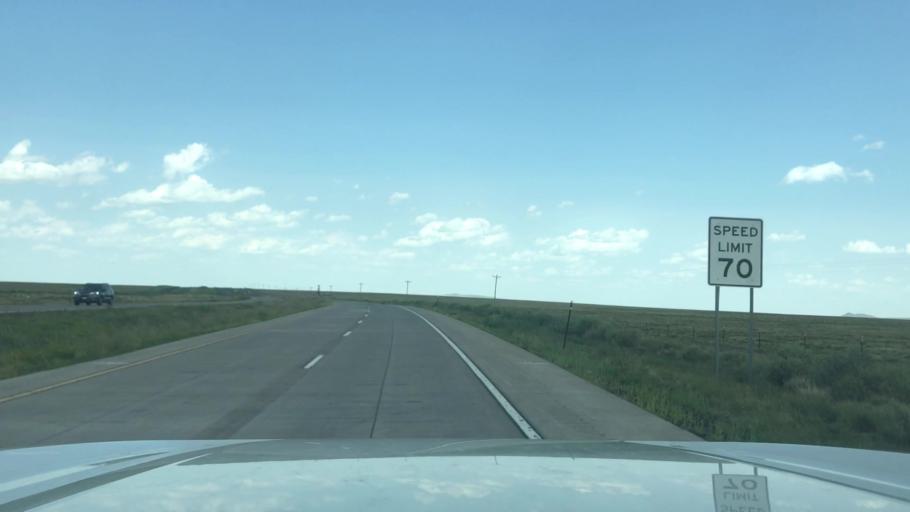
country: US
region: New Mexico
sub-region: Union County
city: Clayton
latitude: 36.6139
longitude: -103.6826
